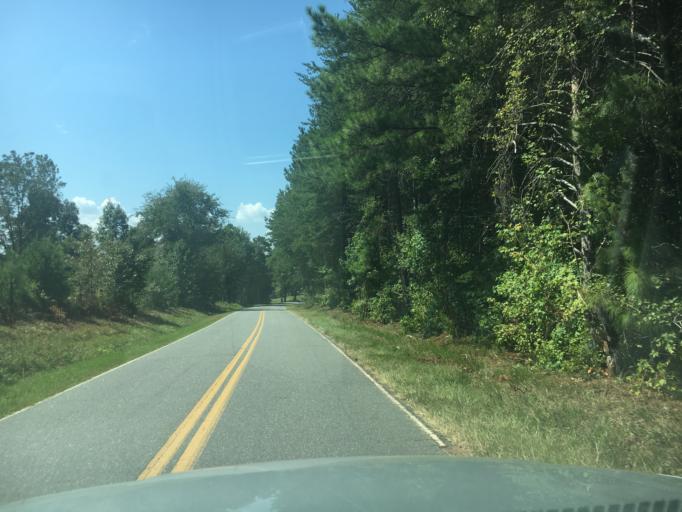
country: US
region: South Carolina
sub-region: Spartanburg County
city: Landrum
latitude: 35.1958
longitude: -82.0334
